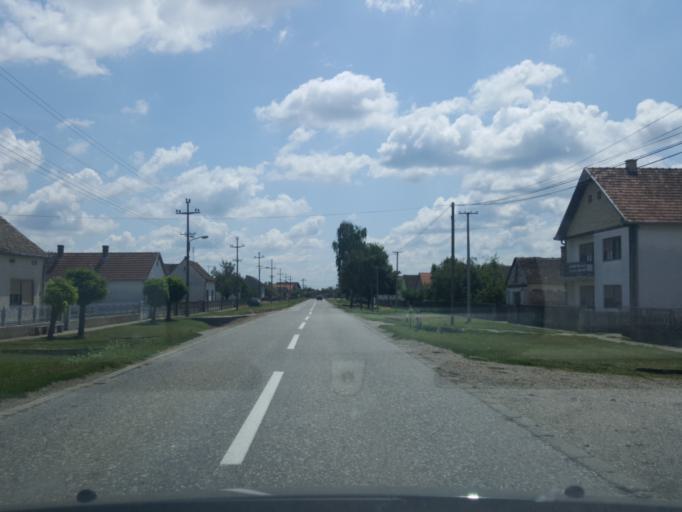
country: RS
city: Glusci
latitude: 44.8834
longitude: 19.5538
